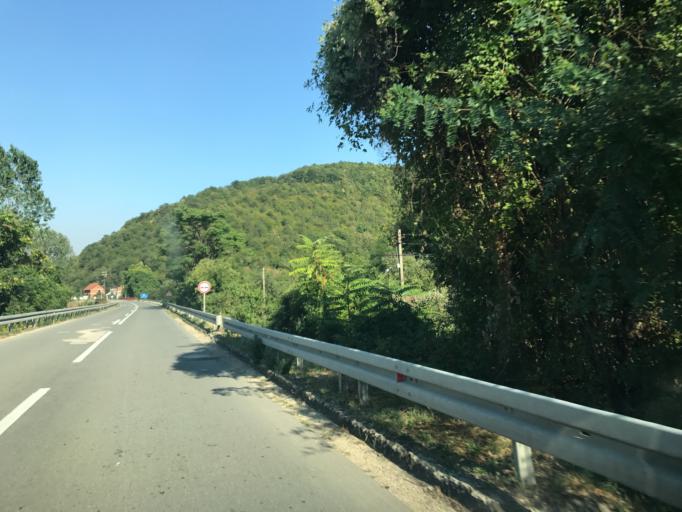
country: RO
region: Caras-Severin
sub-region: Comuna Berzasca
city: Liubcova
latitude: 44.6403
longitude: 21.9055
